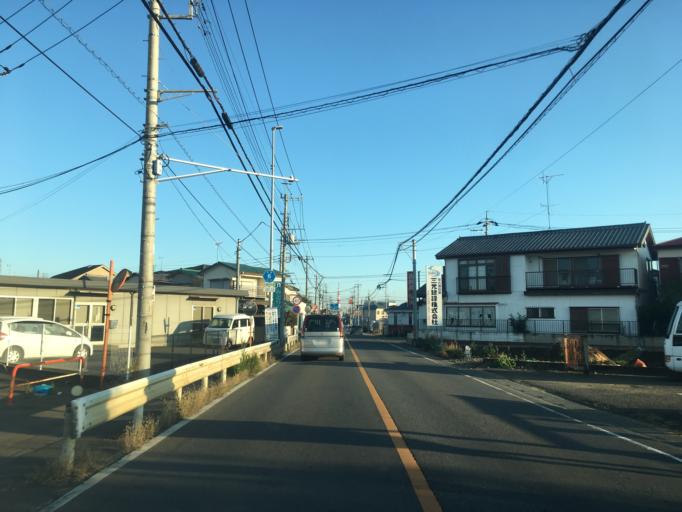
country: JP
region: Saitama
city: Kawagoe
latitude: 35.8850
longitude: 139.4765
